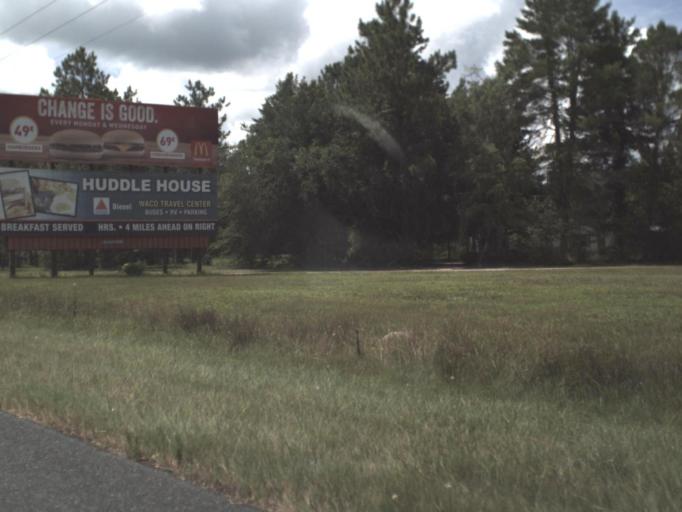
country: US
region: Florida
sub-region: Taylor County
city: Perry
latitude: 30.1506
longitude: -83.6150
